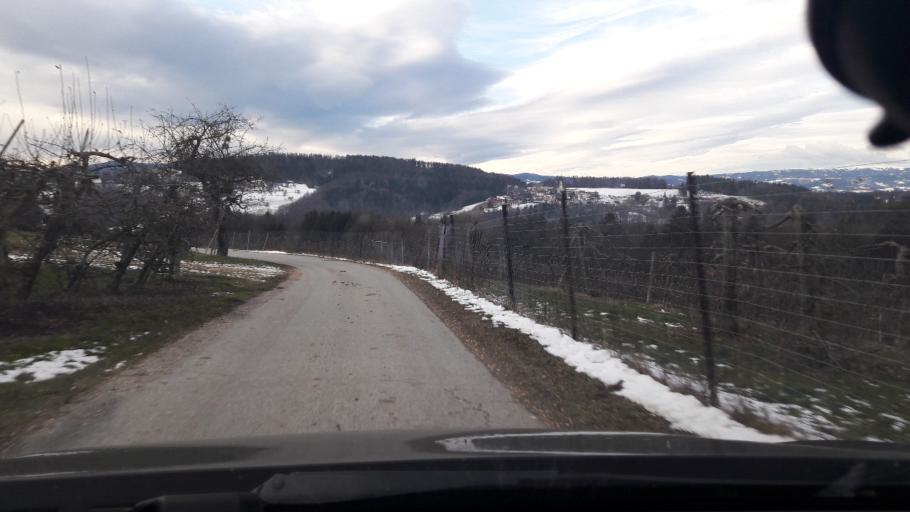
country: AT
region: Styria
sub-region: Politischer Bezirk Graz-Umgebung
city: Sankt Oswald bei Plankenwarth
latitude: 47.0768
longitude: 15.2744
